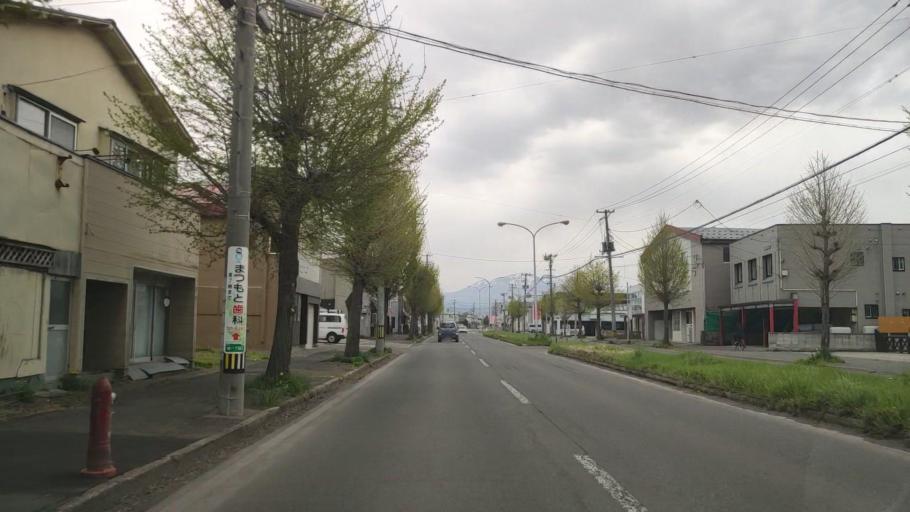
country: JP
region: Aomori
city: Aomori Shi
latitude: 40.8199
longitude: 140.7727
